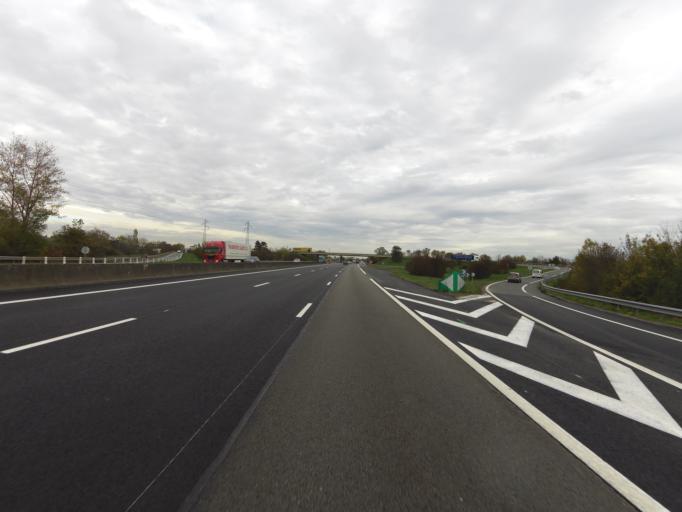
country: FR
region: Rhone-Alpes
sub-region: Departement du Rhone
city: Belleville
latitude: 46.0989
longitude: 4.7493
